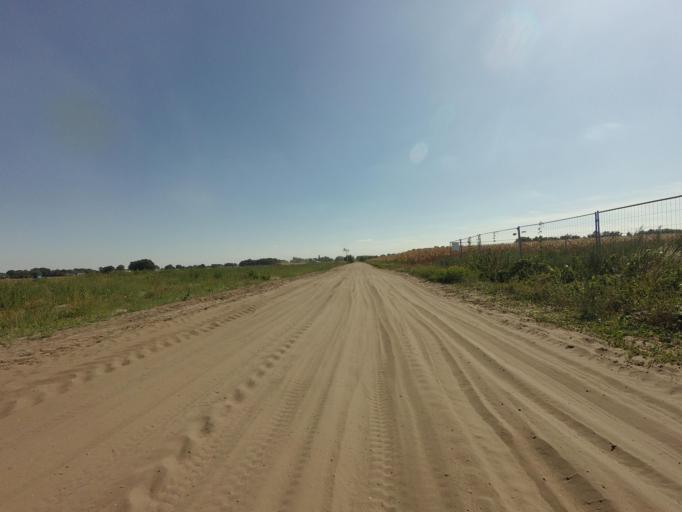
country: NL
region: North Brabant
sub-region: Gemeente Someren
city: Someren
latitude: 51.3842
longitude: 5.6687
